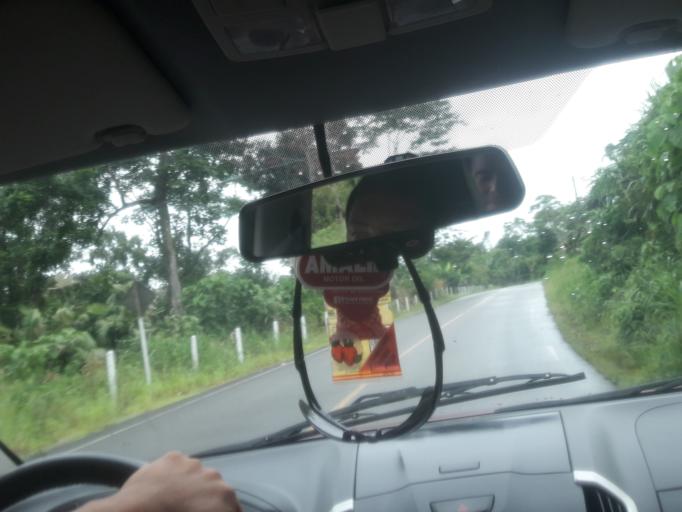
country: EC
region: Napo
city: Tena
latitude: -1.0353
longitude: -77.6890
